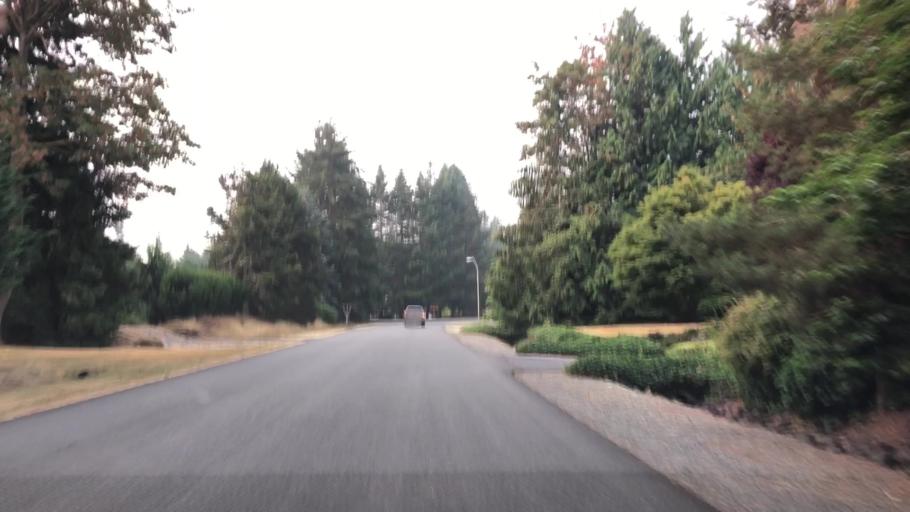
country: US
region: Washington
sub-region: King County
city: Cottage Lake
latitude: 47.7184
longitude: -122.1065
